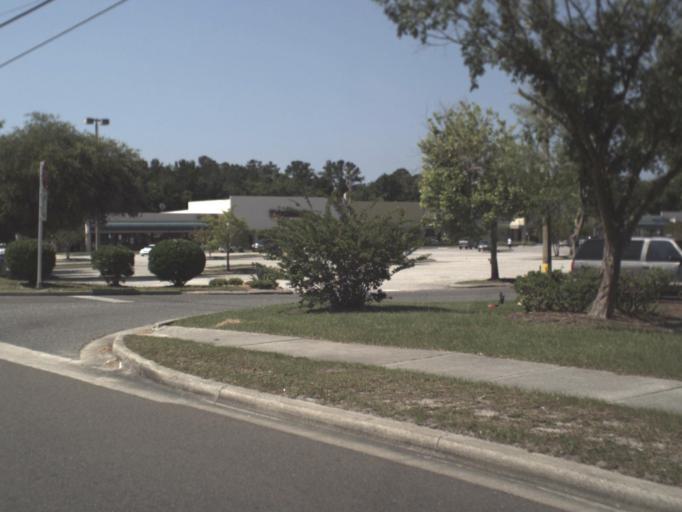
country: US
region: Florida
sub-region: Duval County
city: Jacksonville
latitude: 30.4378
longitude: -81.6976
